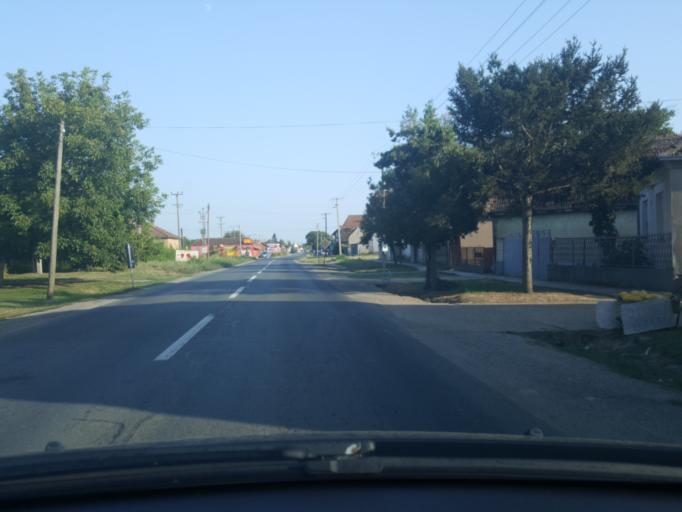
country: RS
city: Platicevo
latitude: 44.8281
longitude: 19.7782
